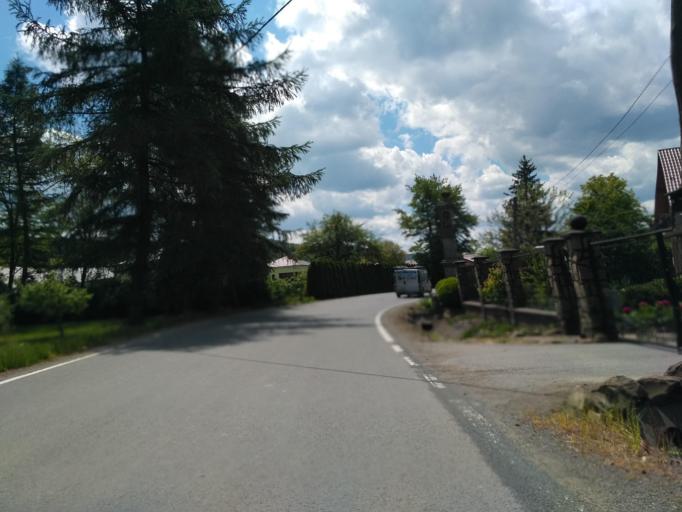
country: PL
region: Subcarpathian Voivodeship
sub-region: Powiat krosnienski
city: Dukla
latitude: 49.5763
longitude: 21.6965
